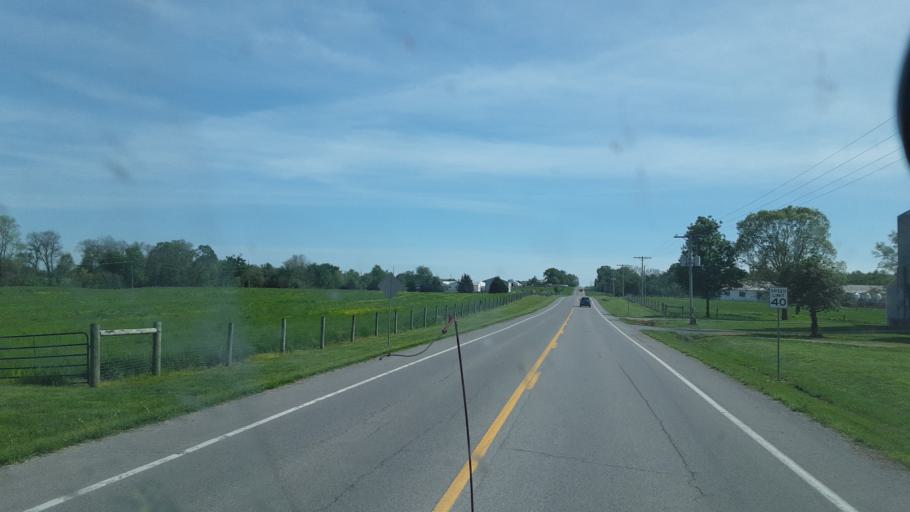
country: US
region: Illinois
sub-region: Jackson County
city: Carbondale
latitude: 37.7001
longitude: -89.2471
